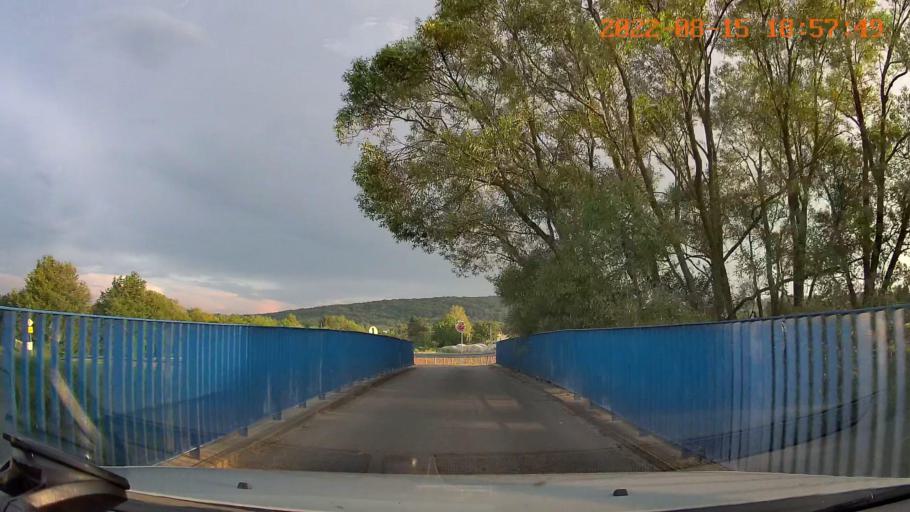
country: PL
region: Lesser Poland Voivodeship
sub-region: Powiat krakowski
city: Rzaska
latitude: 50.0779
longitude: 19.8485
